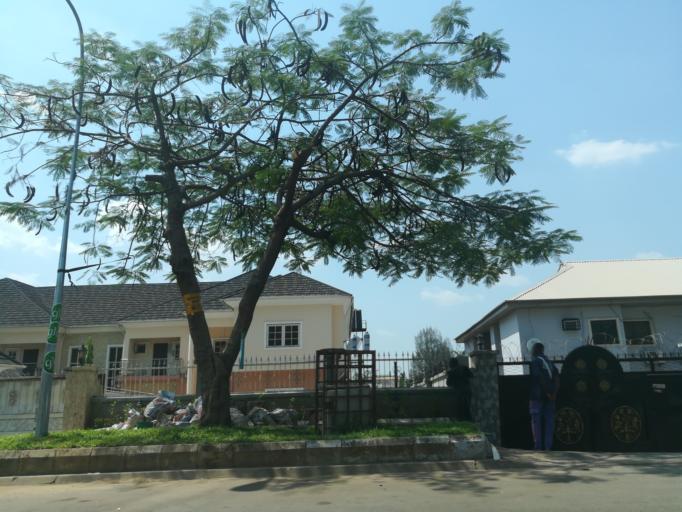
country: NG
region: Abuja Federal Capital Territory
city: Abuja
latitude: 9.0638
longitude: 7.4378
